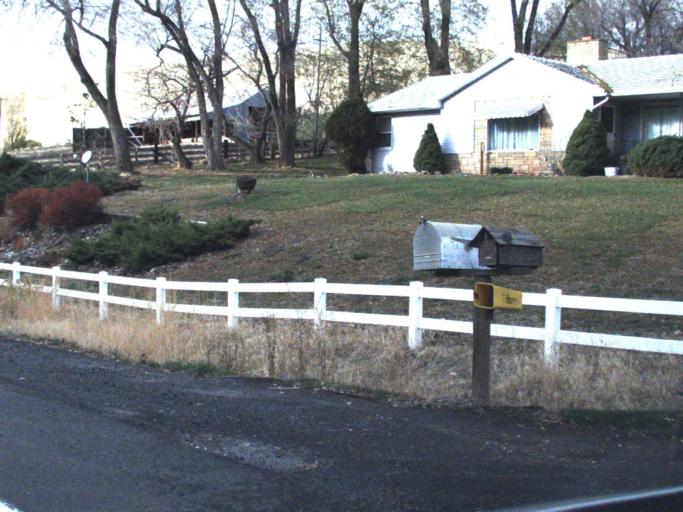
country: US
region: Washington
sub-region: Garfield County
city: Pomeroy
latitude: 46.4739
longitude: -117.5418
